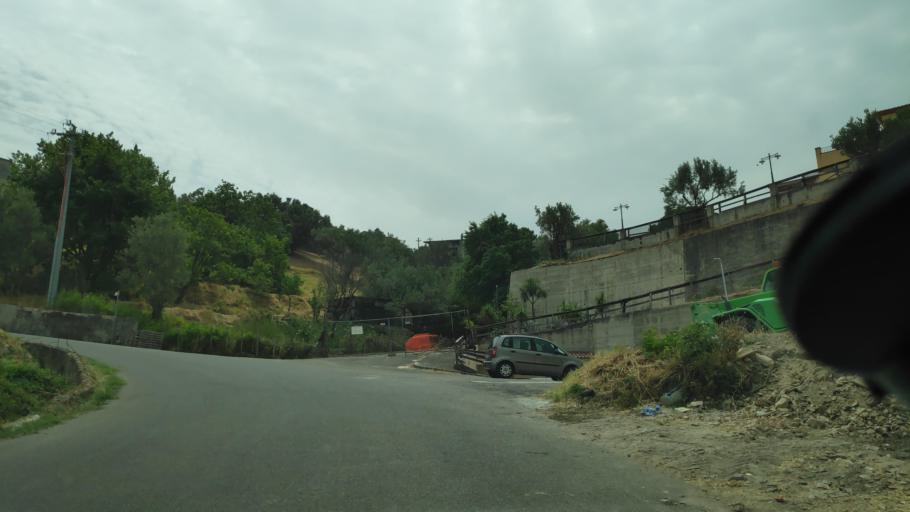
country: IT
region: Calabria
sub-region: Provincia di Catanzaro
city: Davoli
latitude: 38.6505
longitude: 16.4885
